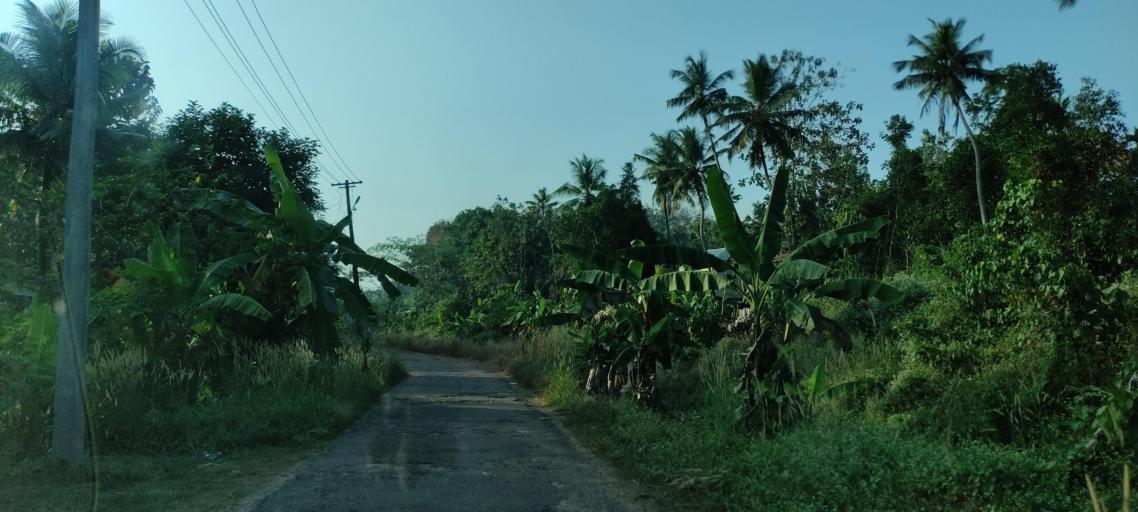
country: IN
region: Kerala
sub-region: Pattanamtitta
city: Adur
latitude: 9.1351
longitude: 76.7323
